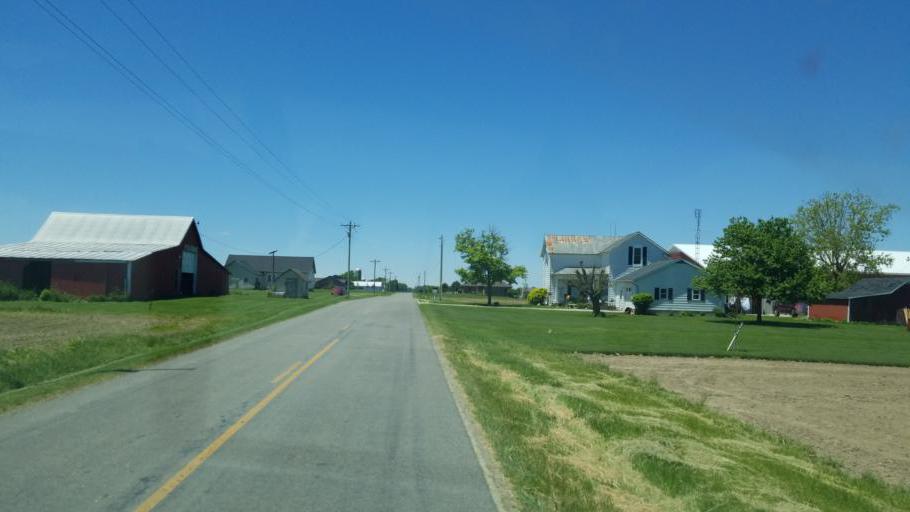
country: US
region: Ohio
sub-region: Mercer County
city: Fort Recovery
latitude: 40.3668
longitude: -84.7331
